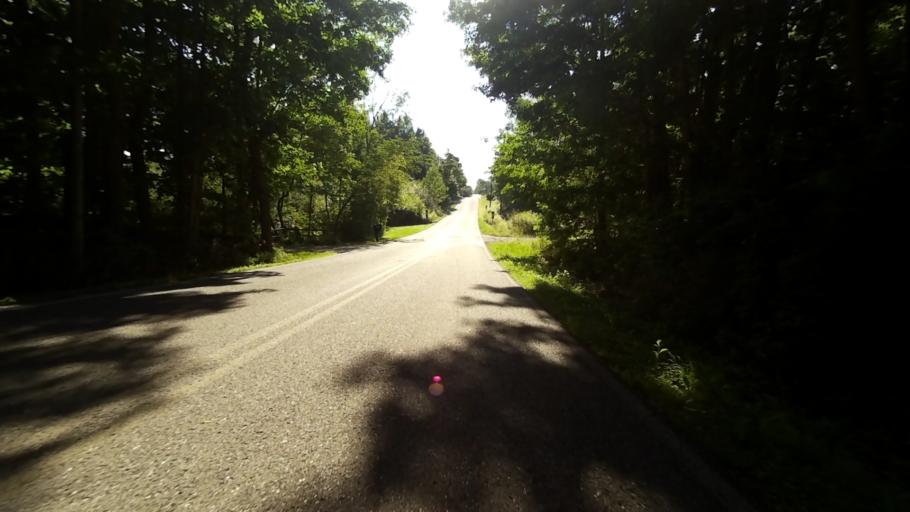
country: US
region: Ohio
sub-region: Portage County
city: Aurora
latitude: 41.2997
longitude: -81.2966
